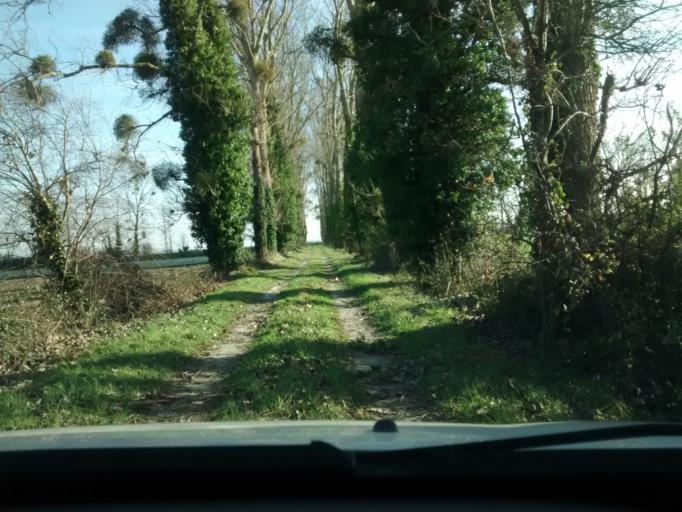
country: FR
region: Brittany
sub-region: Departement d'Ille-et-Vilaine
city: Roz-sur-Couesnon
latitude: 48.6108
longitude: -1.5963
